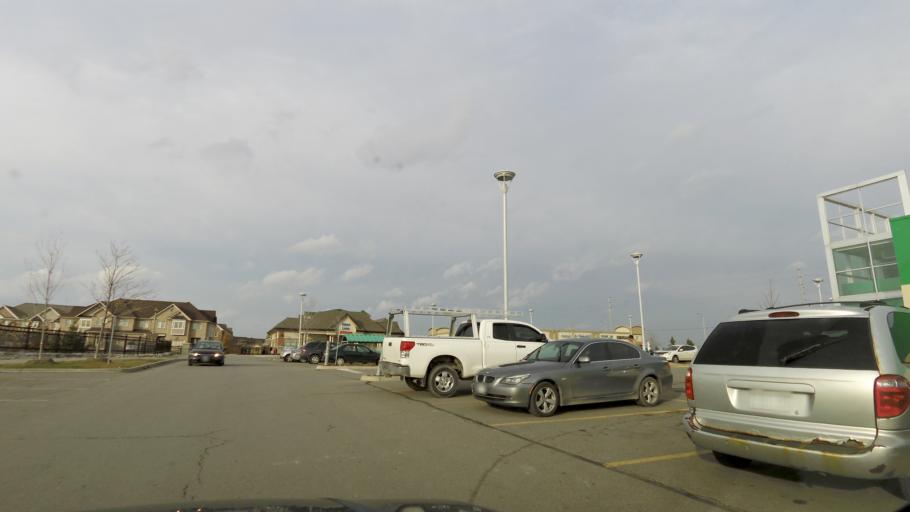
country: CA
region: Ontario
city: Brampton
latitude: 43.7740
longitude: -79.6541
